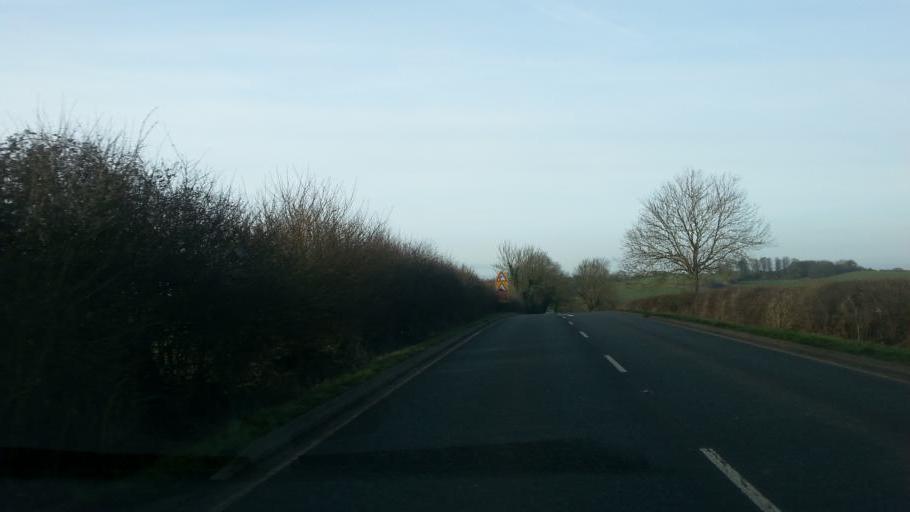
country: GB
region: England
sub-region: Leicestershire
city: Wymondham
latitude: 52.8499
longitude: -0.7711
